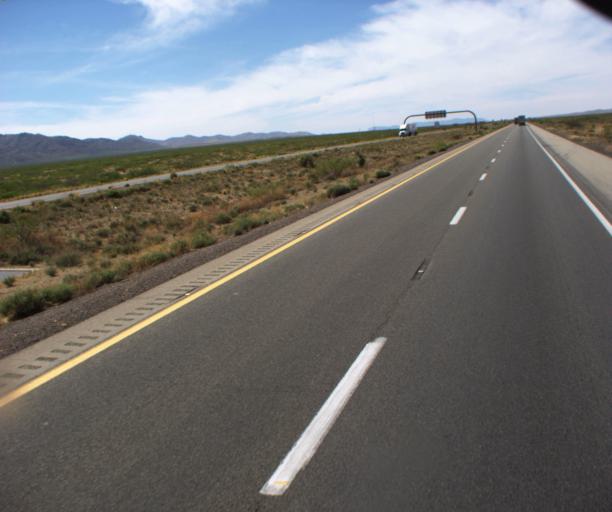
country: US
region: Arizona
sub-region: Cochise County
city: Willcox
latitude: 32.3334
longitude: -109.5233
